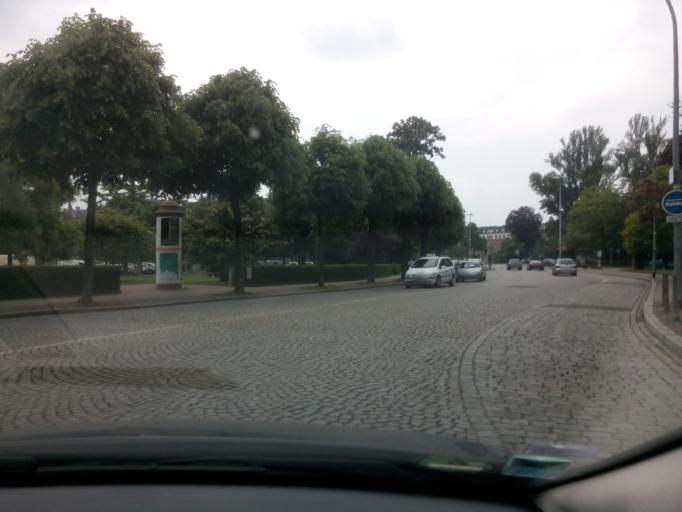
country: FR
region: Alsace
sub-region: Departement du Bas-Rhin
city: Strasbourg
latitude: 48.5857
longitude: 7.7624
